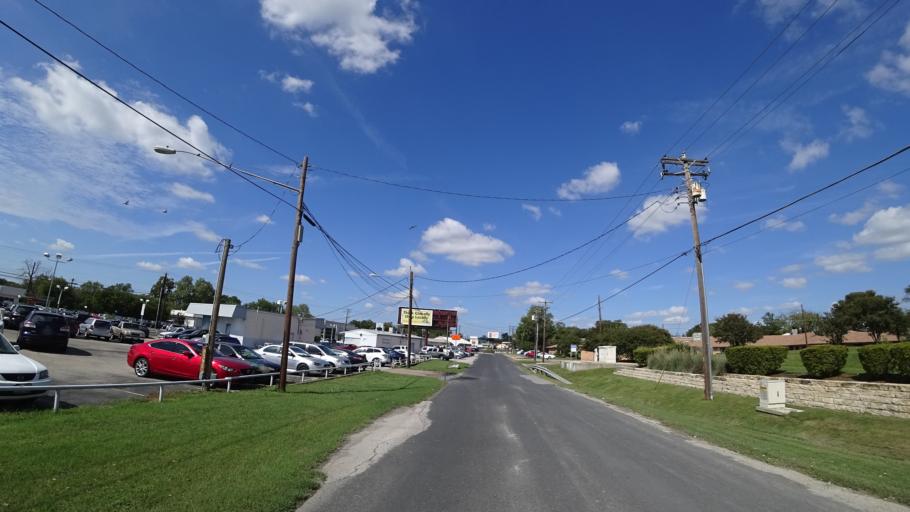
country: US
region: Texas
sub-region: Travis County
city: Austin
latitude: 30.3453
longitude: -97.7367
